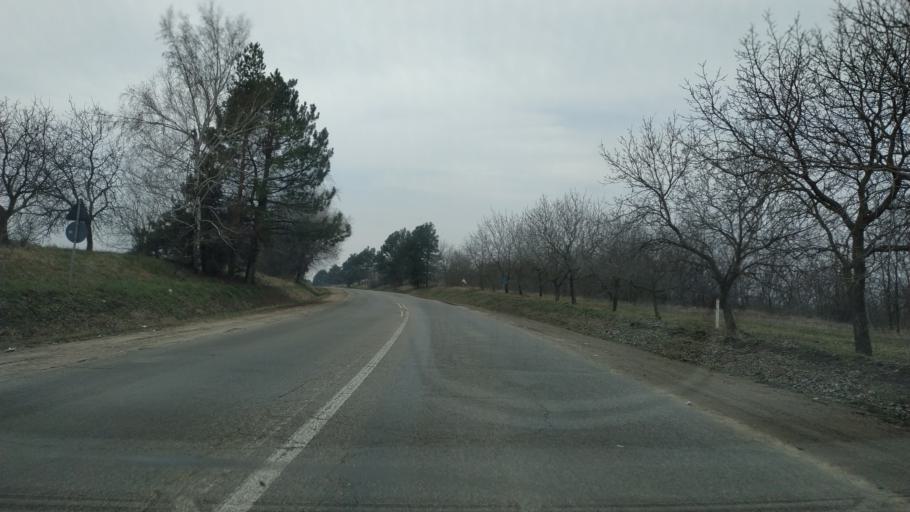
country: MD
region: Cahul
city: Cahul
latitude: 45.9471
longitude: 28.3148
